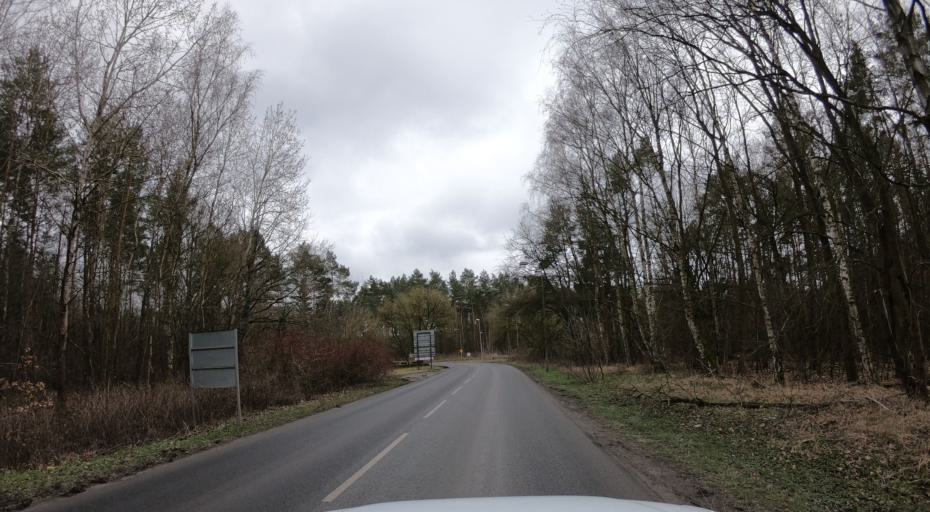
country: PL
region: West Pomeranian Voivodeship
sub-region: Powiat policki
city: Police
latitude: 53.5470
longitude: 14.5030
